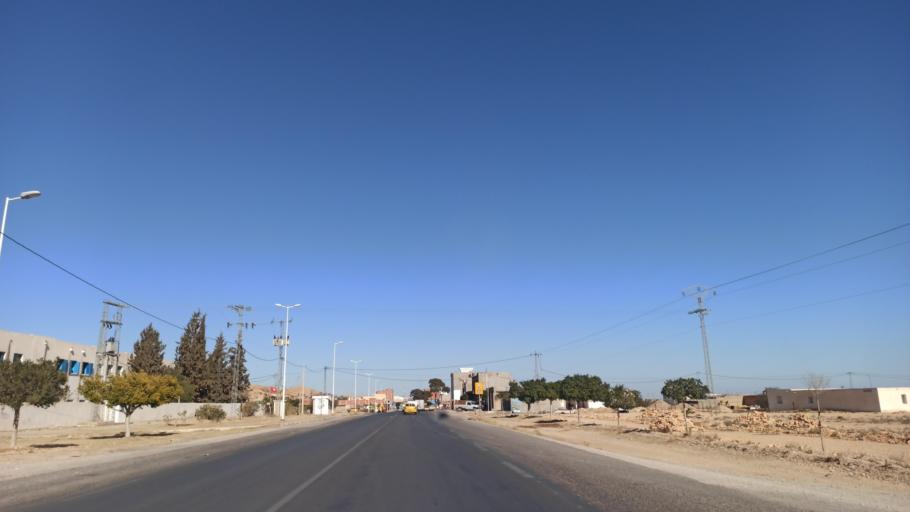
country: TN
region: Sidi Bu Zayd
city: Bi'r al Hufayy
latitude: 34.9157
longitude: 9.1846
